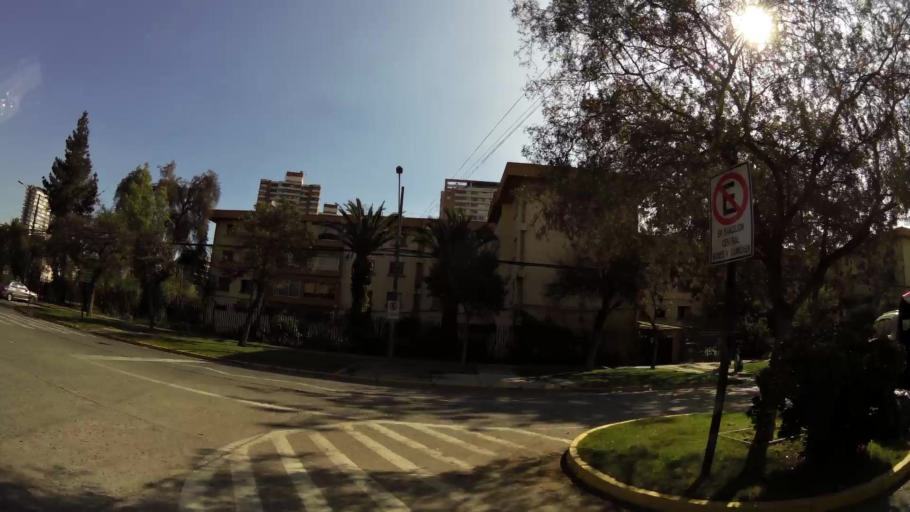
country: CL
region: Santiago Metropolitan
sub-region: Provincia de Santiago
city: Santiago
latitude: -33.4637
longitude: -70.6228
